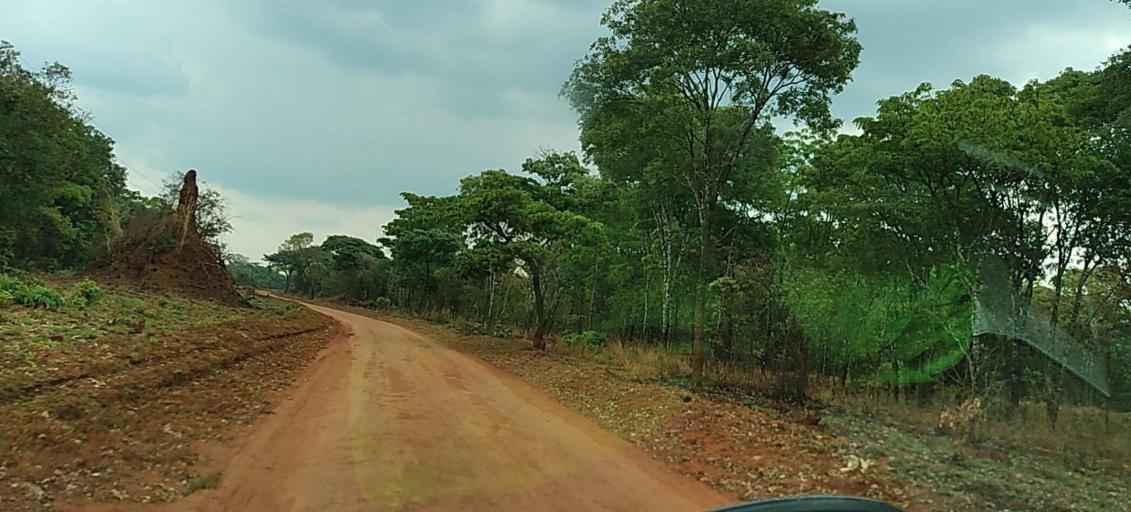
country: ZM
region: North-Western
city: Solwezi
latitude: -12.7811
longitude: 26.4888
